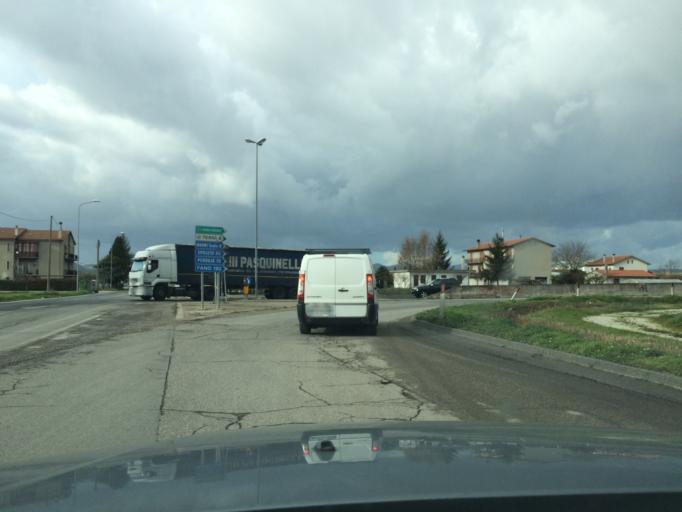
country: IT
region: Umbria
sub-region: Provincia di Terni
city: Terni
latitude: 42.5508
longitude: 12.5844
